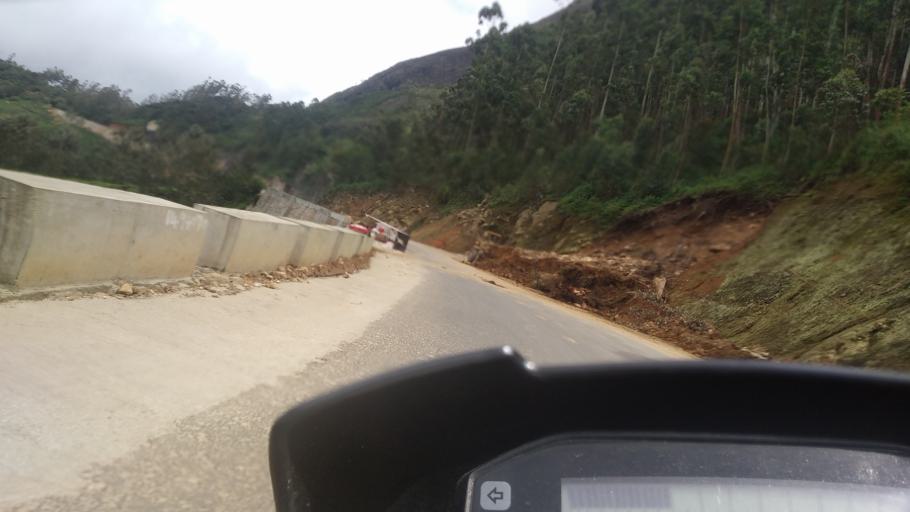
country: IN
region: Kerala
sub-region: Idukki
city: Munnar
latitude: 10.0370
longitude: 77.1153
